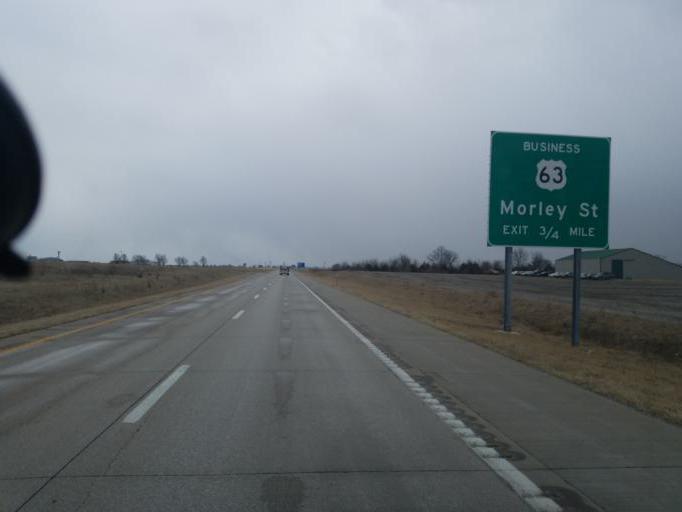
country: US
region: Missouri
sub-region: Randolph County
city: Moberly
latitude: 39.4701
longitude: -92.4350
